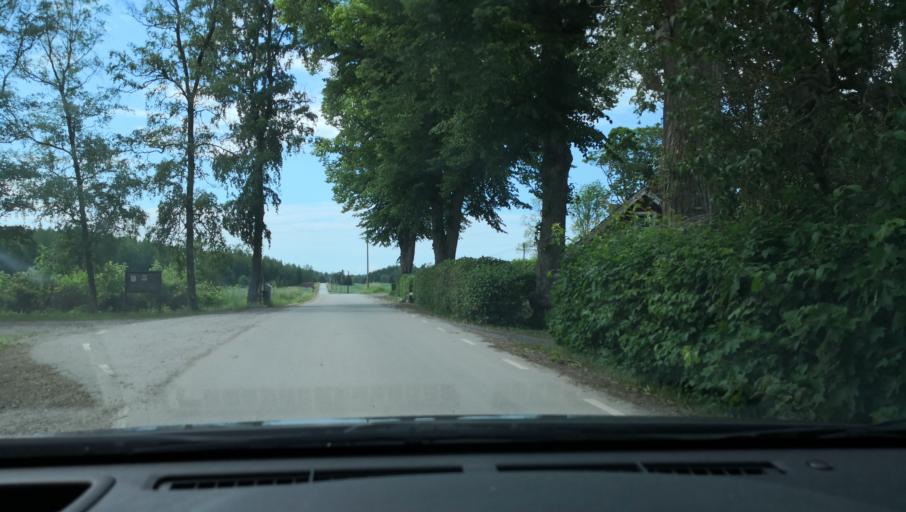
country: SE
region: Uppsala
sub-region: Habo Kommun
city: Balsta
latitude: 59.7105
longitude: 17.4869
